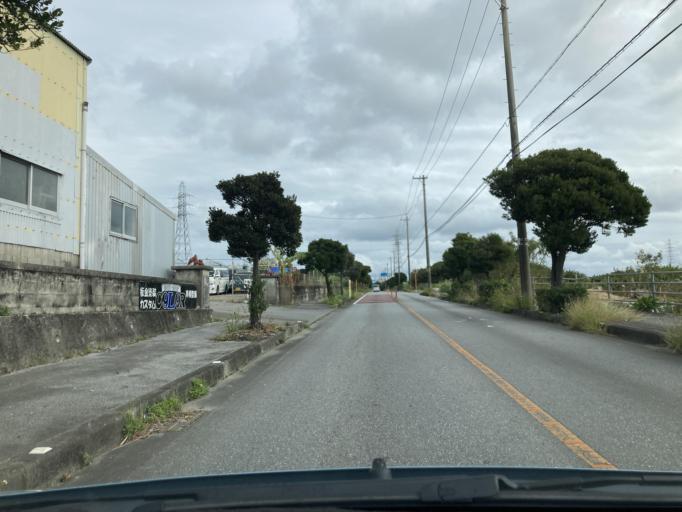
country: JP
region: Okinawa
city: Itoman
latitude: 26.1199
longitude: 127.6849
